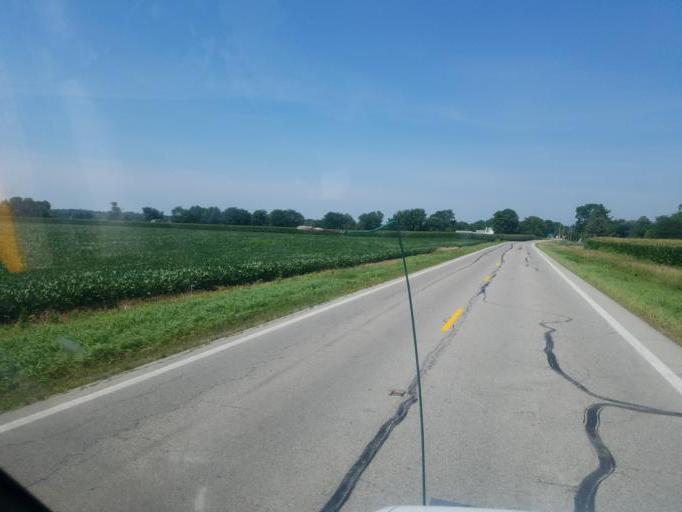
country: US
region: Ohio
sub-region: Logan County
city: West Liberty
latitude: 40.2514
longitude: -83.7428
